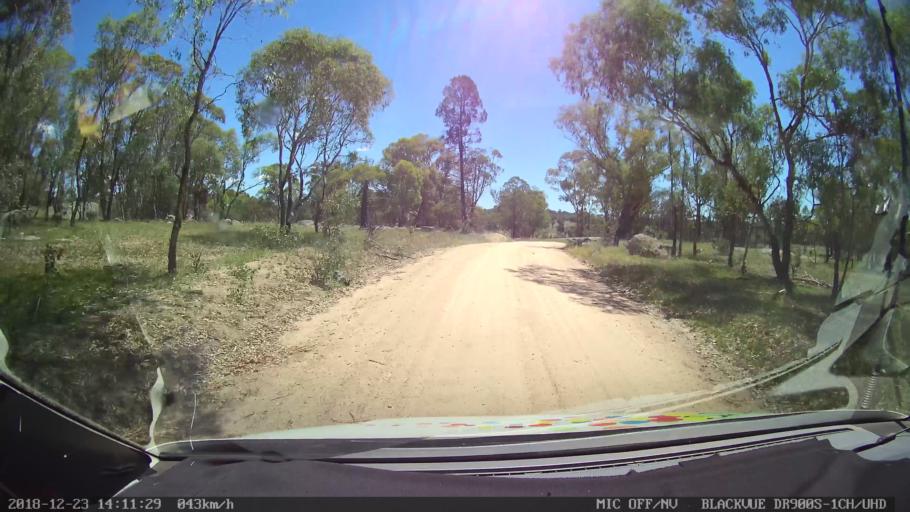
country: AU
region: New South Wales
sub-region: Tamworth Municipality
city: Manilla
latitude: -30.6517
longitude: 151.0504
